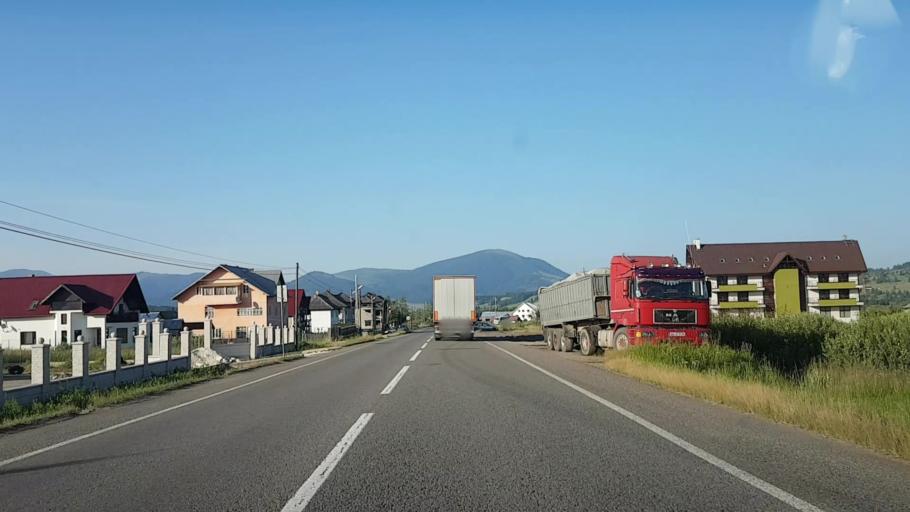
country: RO
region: Suceava
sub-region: Comuna Poiana Stampei
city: Poiana Stampei
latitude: 47.3272
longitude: 25.1444
